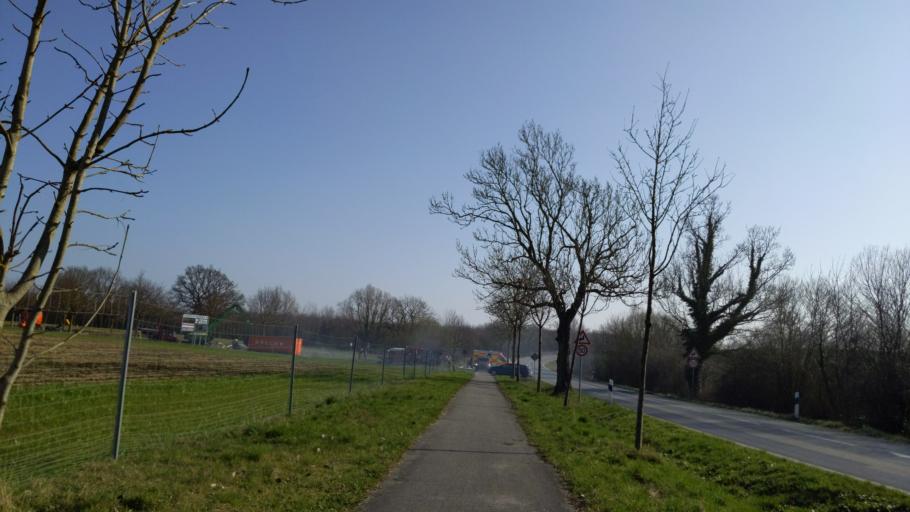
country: DE
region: Schleswig-Holstein
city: Altenkrempe
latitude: 54.1276
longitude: 10.8483
